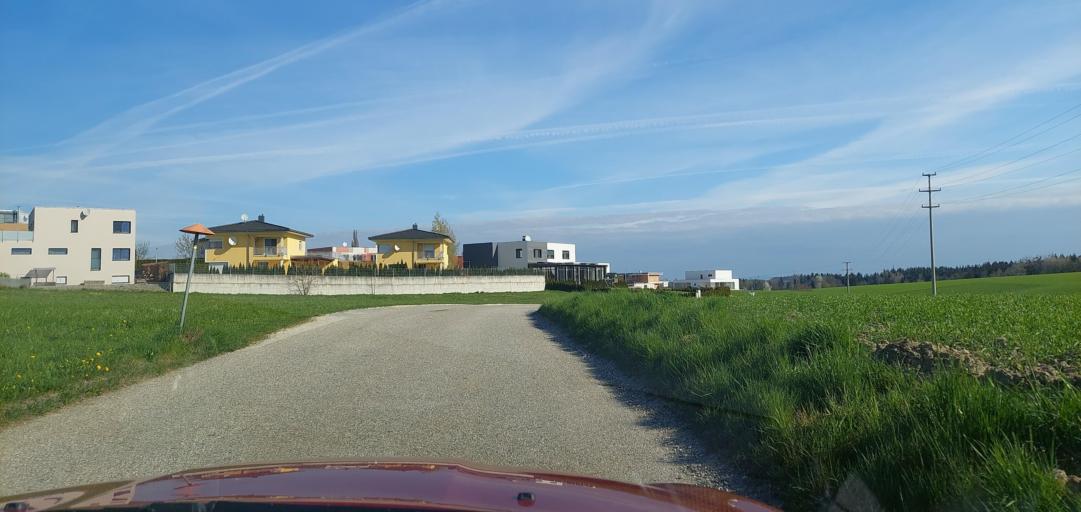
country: AT
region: Upper Austria
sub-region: Politischer Bezirk Ried im Innkreis
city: Ried im Innkreis
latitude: 48.2003
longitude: 13.5069
